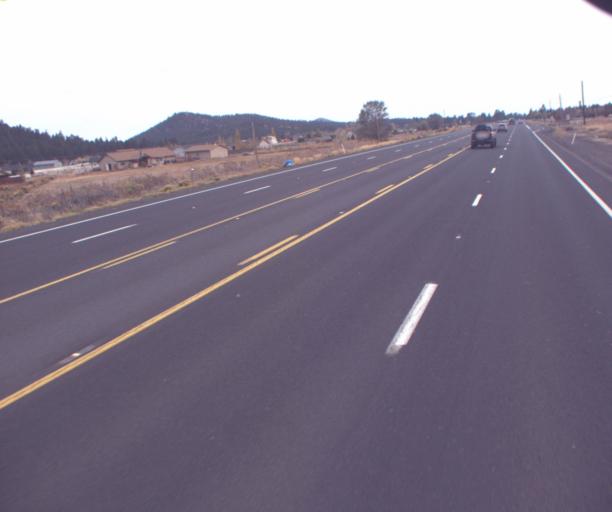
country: US
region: Arizona
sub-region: Coconino County
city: Flagstaff
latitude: 35.3008
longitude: -111.5429
